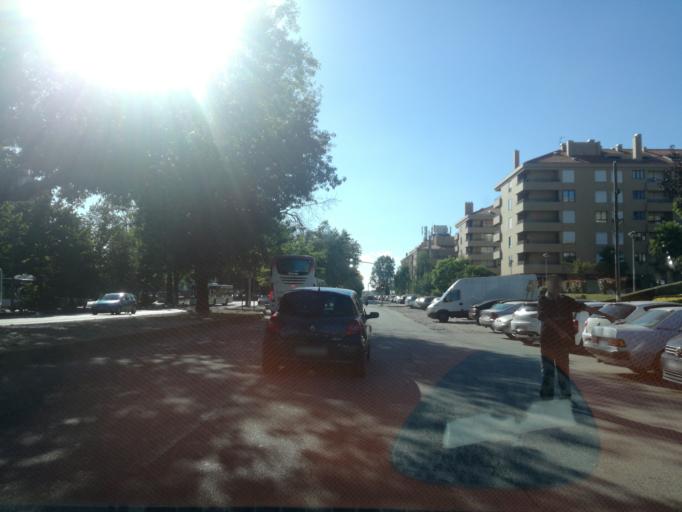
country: PT
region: Porto
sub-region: Matosinhos
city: Sao Mamede de Infesta
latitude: 41.1837
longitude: -8.6023
